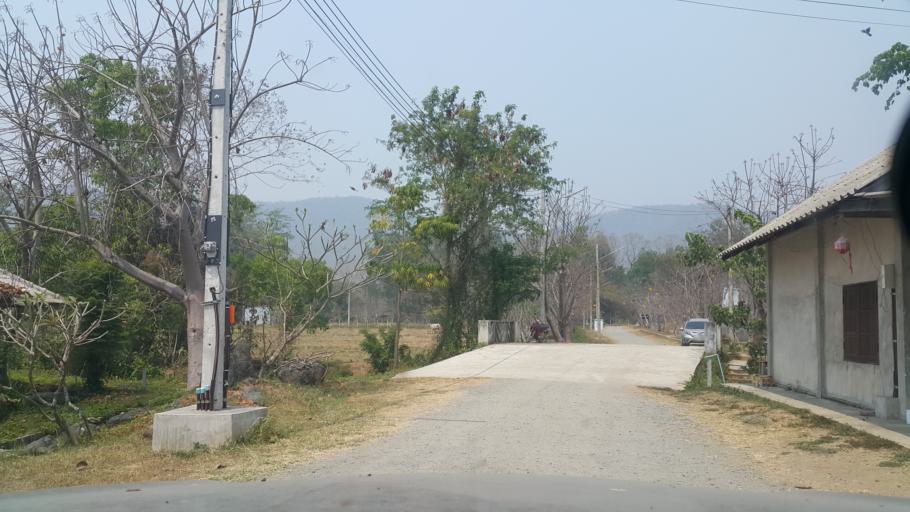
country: TH
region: Chiang Mai
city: Mae On
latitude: 18.7409
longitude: 99.2148
